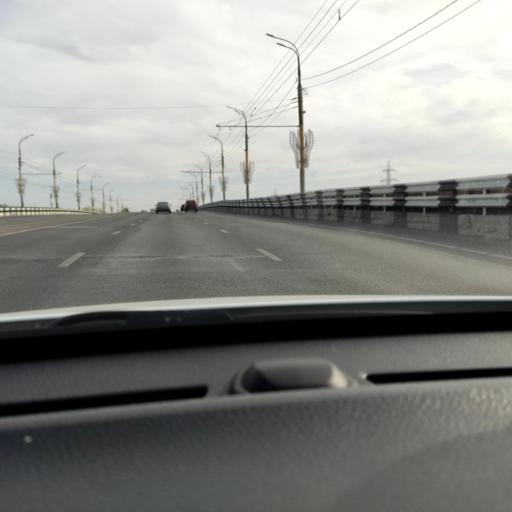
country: RU
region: Voronezj
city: Voronezh
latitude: 51.6343
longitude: 39.2202
